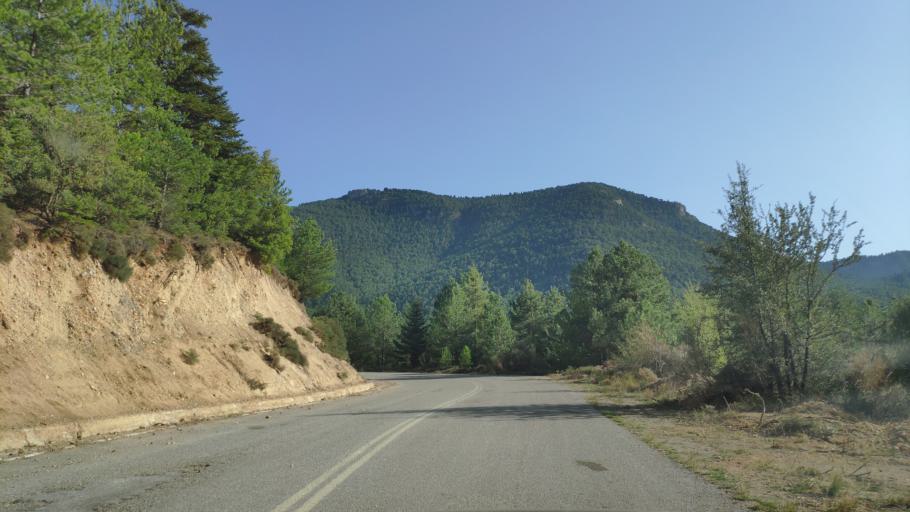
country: GR
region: West Greece
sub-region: Nomos Achaias
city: Aiyira
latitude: 38.0005
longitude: 22.3833
